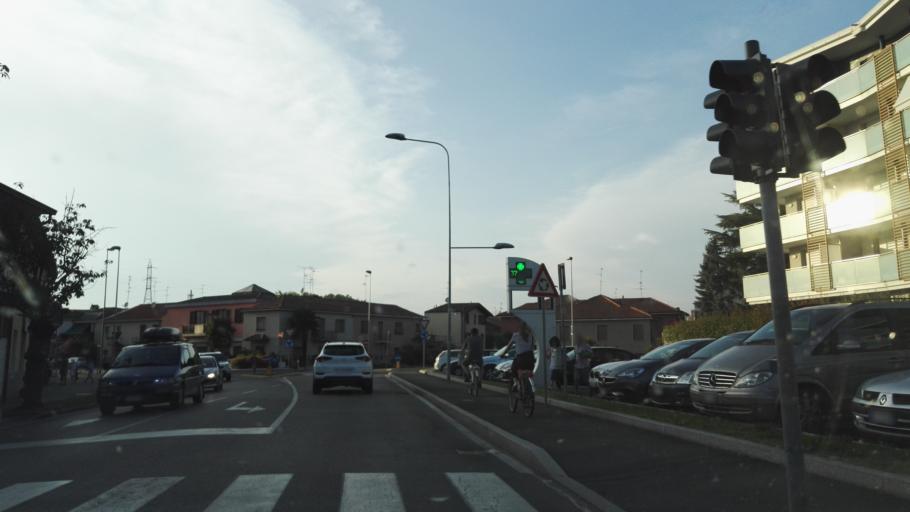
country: IT
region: Lombardy
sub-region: Citta metropolitana di Milano
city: Paullo
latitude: 45.4179
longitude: 9.3966
